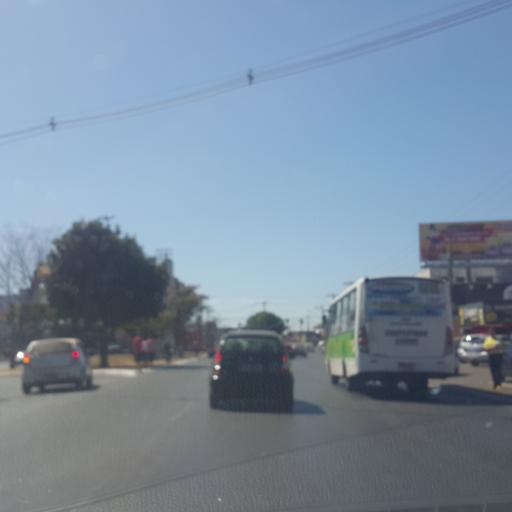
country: BR
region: Federal District
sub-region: Brasilia
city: Brasilia
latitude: -15.8035
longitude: -48.0690
